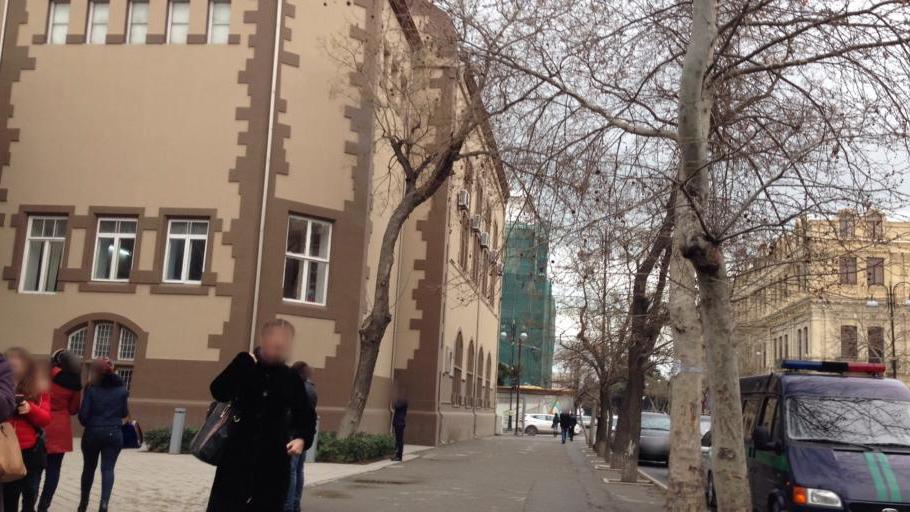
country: AZ
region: Baki
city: Baku
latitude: 40.3730
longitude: 49.8477
